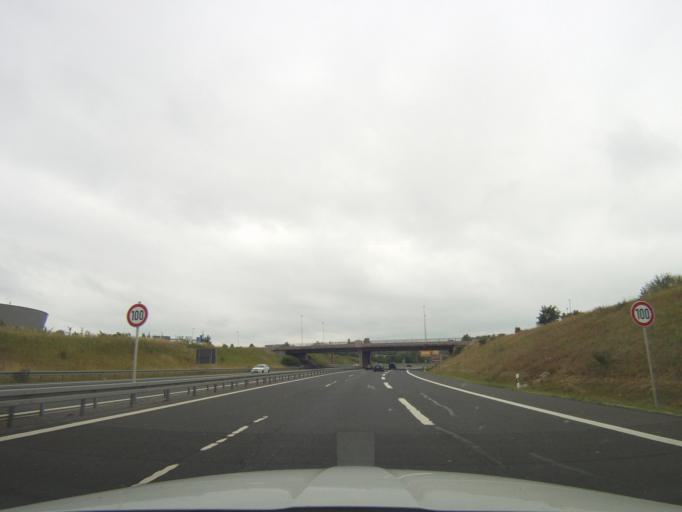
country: DE
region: Bavaria
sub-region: Upper Franconia
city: Coburg
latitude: 50.2881
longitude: 10.9785
